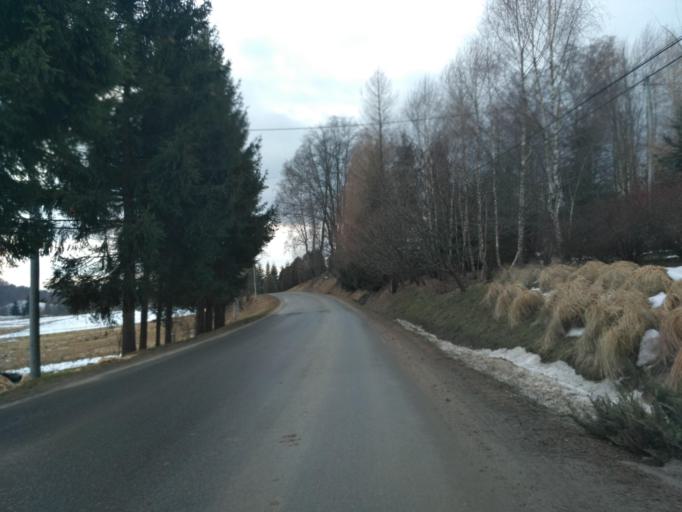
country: PL
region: Subcarpathian Voivodeship
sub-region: Powiat brzozowski
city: Dydnia
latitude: 49.6240
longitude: 22.1547
